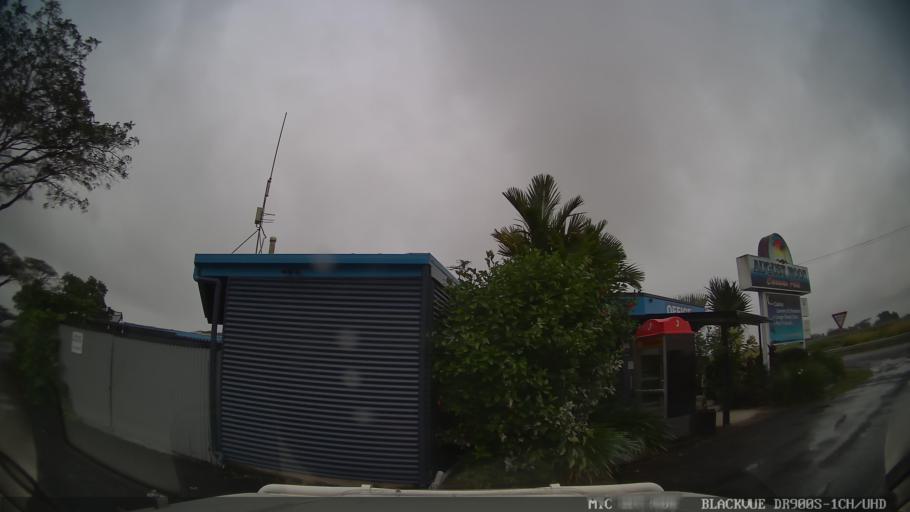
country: AU
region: Queensland
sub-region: Cassowary Coast
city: Innisfail
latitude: -17.5518
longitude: 146.0331
